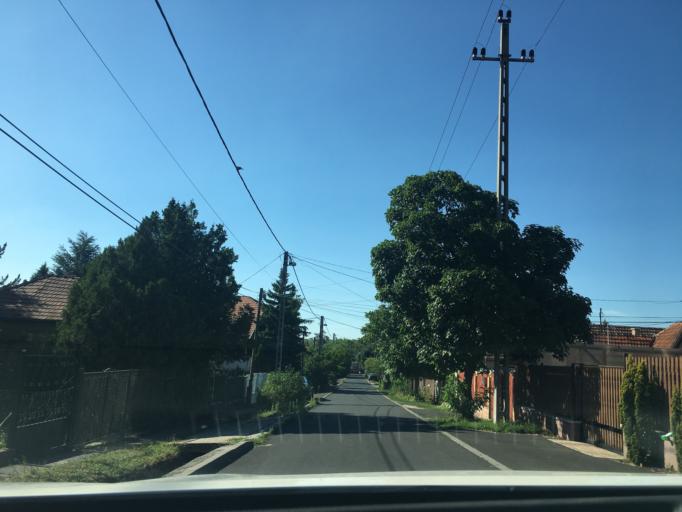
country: HU
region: Budapest
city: Budapest XVII. keruelet
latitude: 47.4802
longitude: 19.2722
